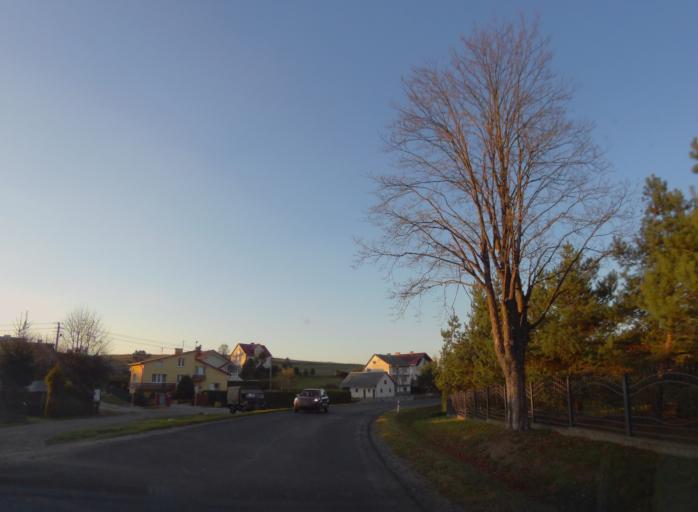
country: PL
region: Subcarpathian Voivodeship
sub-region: Powiat leski
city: Lesko
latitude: 49.4081
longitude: 22.3589
